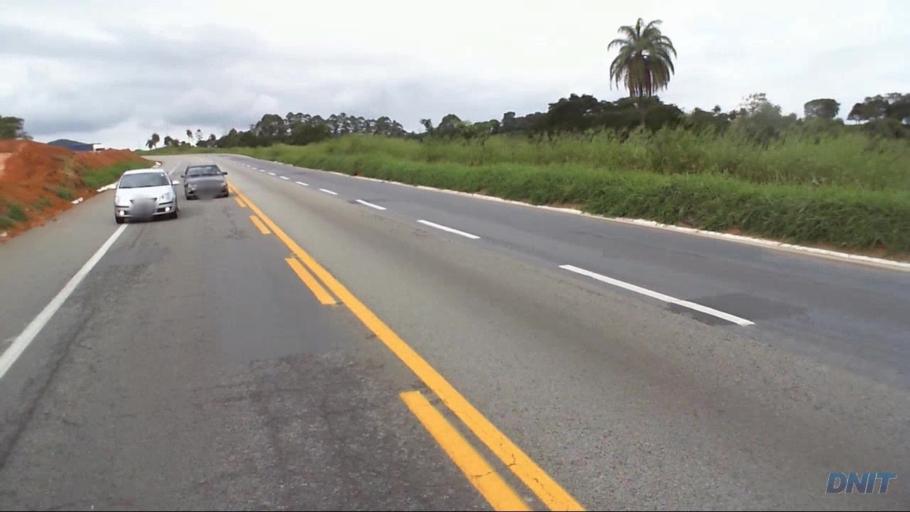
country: BR
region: Minas Gerais
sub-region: Caete
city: Caete
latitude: -19.7264
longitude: -43.5670
